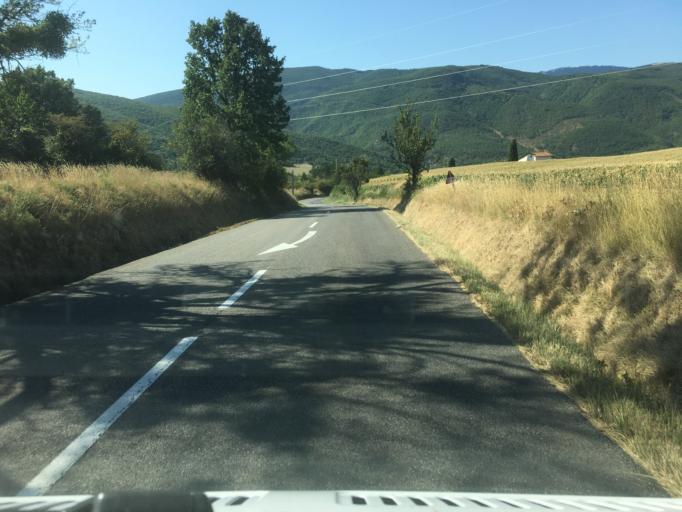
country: FR
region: Provence-Alpes-Cote d'Azur
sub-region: Departement des Alpes-de-Haute-Provence
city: Sisteron
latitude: 44.1813
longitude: 5.9320
